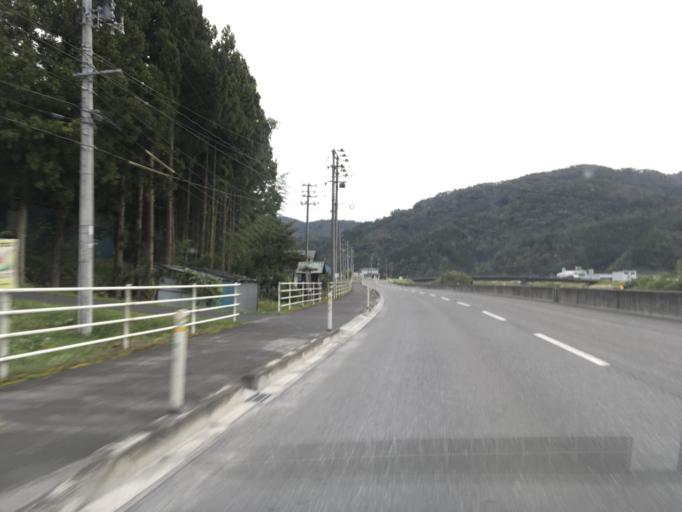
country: JP
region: Iwate
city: Ichinoseki
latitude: 38.9794
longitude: 141.2439
